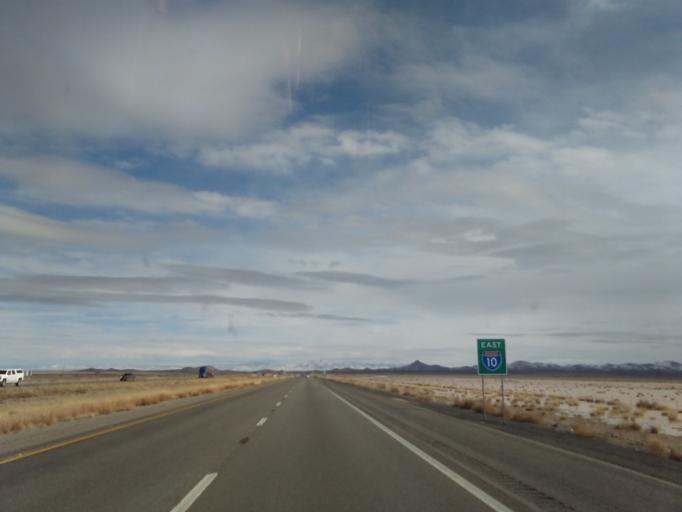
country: US
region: New Mexico
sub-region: Hidalgo County
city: Lordsburg
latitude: 32.2836
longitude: -108.8741
